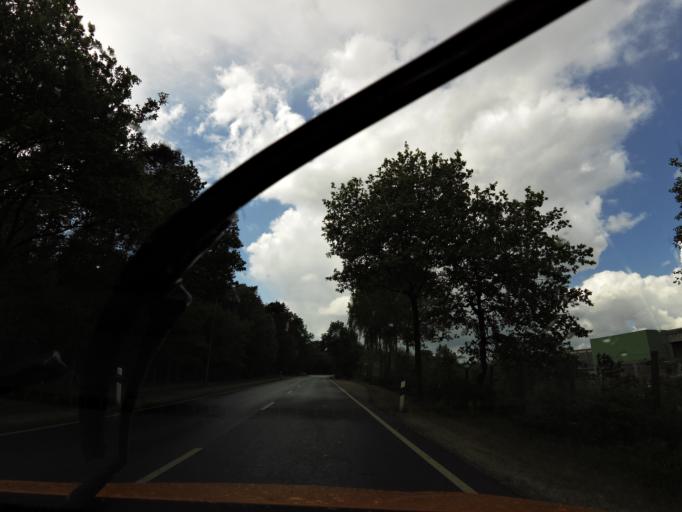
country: DE
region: Lower Saxony
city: Hude
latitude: 53.1009
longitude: 8.4821
